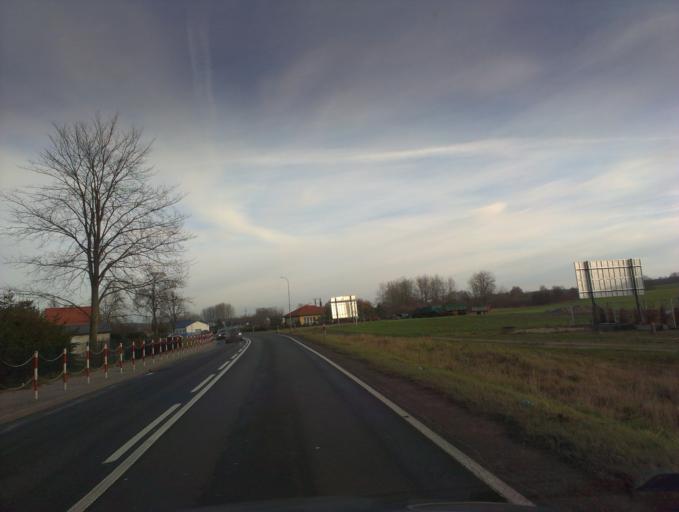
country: PL
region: West Pomeranian Voivodeship
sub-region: Powiat szczecinecki
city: Szczecinek
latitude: 53.7187
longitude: 16.7474
